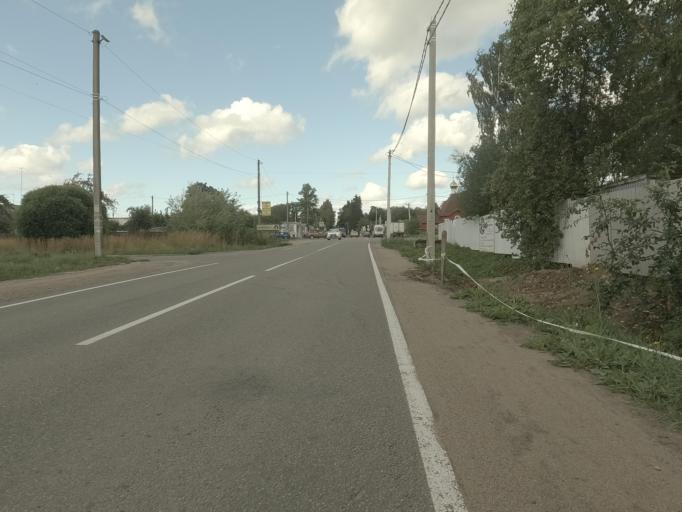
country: RU
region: Leningrad
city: Shcheglovo
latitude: 60.0279
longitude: 30.7549
